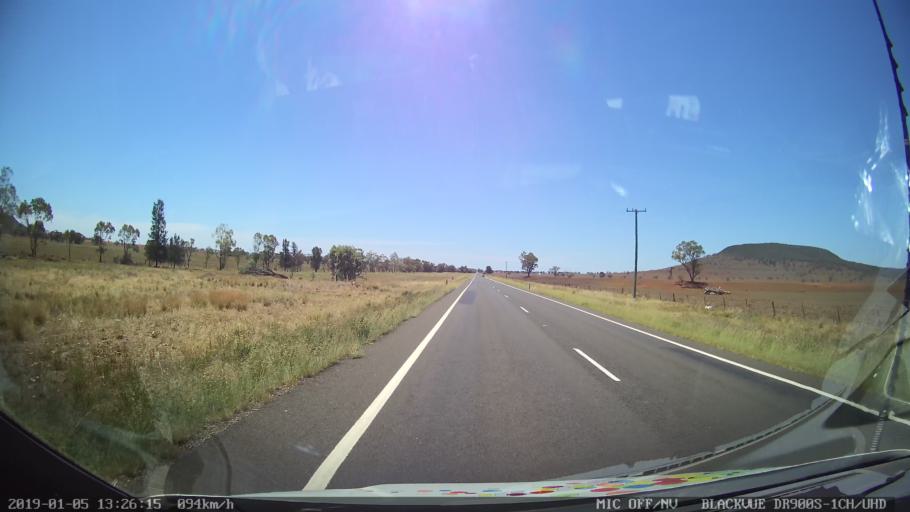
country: AU
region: New South Wales
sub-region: Gunnedah
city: Gunnedah
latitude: -31.0546
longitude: 150.0130
